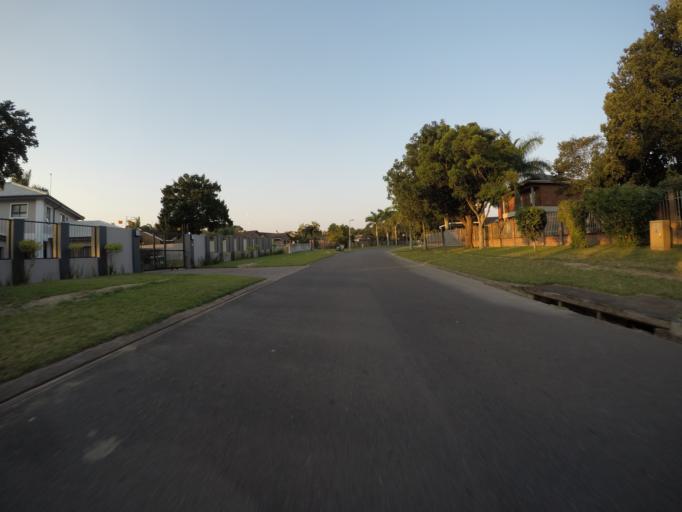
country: ZA
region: KwaZulu-Natal
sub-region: uThungulu District Municipality
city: Richards Bay
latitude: -28.7670
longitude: 32.1156
